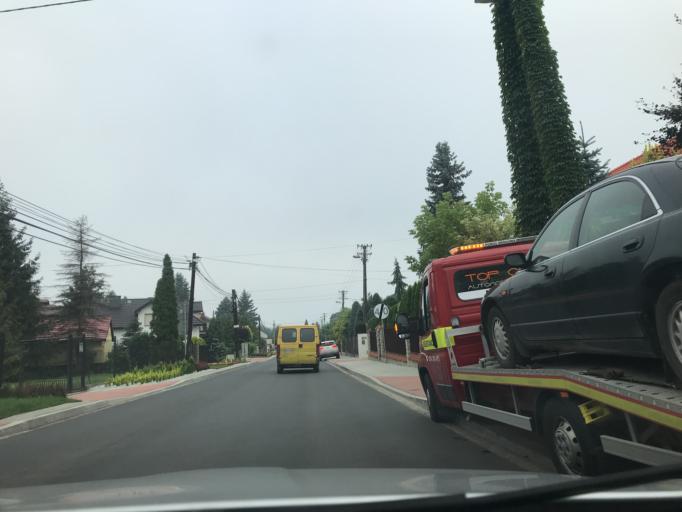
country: PL
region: Lesser Poland Voivodeship
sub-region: Powiat krakowski
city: Ochojno
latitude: 50.0064
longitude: 19.9803
